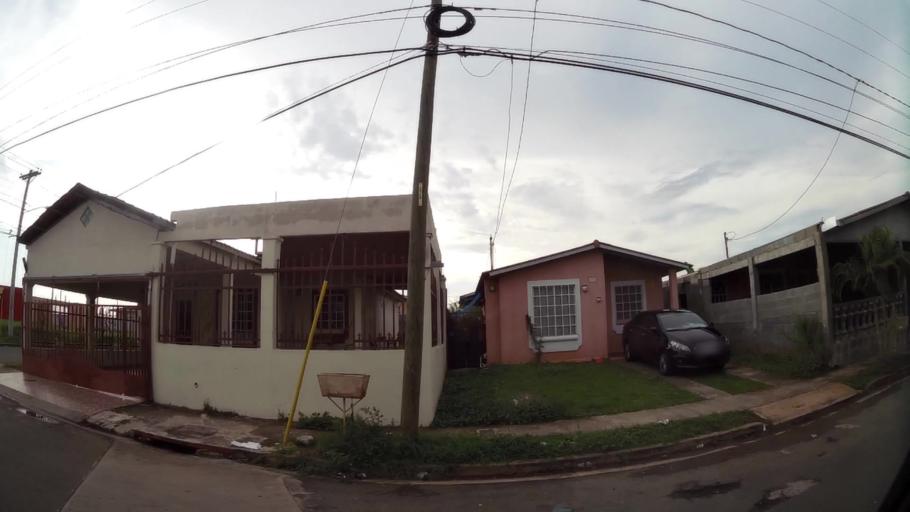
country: PA
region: Panama
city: Tocumen
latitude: 9.0722
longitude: -79.3632
